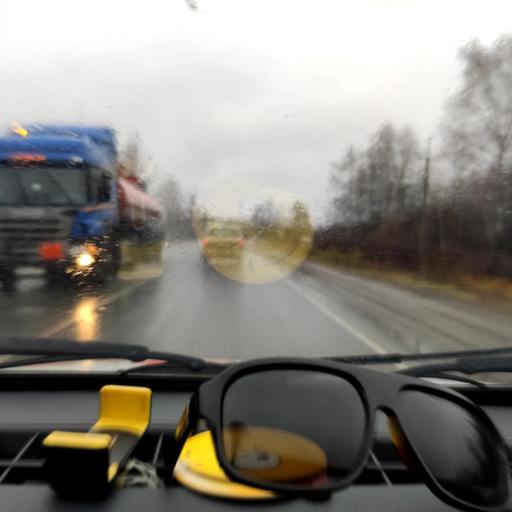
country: RU
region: Bashkortostan
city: Iglino
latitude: 54.8028
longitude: 56.3162
